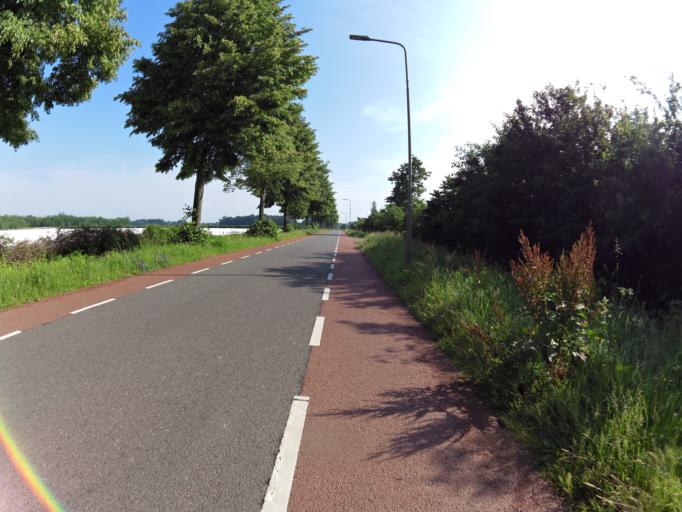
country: NL
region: Limburg
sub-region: Gemeente Maasgouw
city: Maasbracht
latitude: 51.0737
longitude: 5.8824
